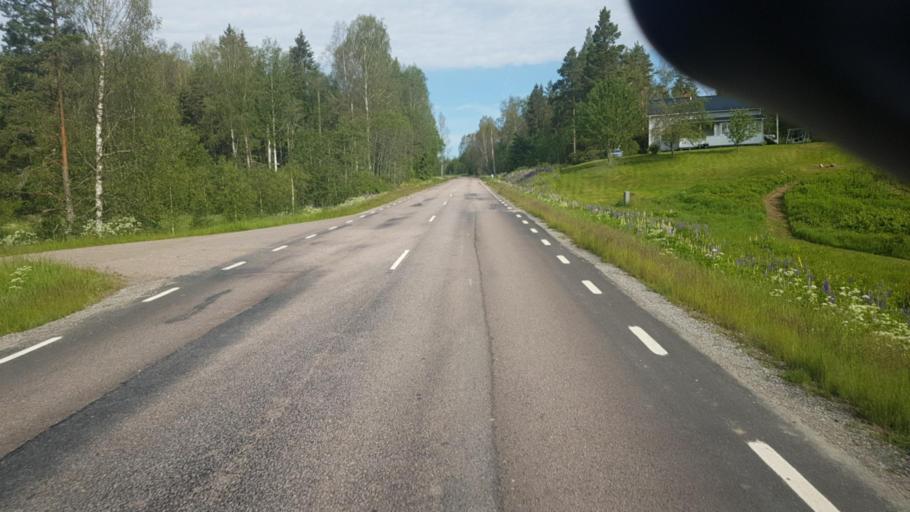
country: SE
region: Vaermland
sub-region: Arvika Kommun
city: Arvika
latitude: 59.8109
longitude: 12.5895
